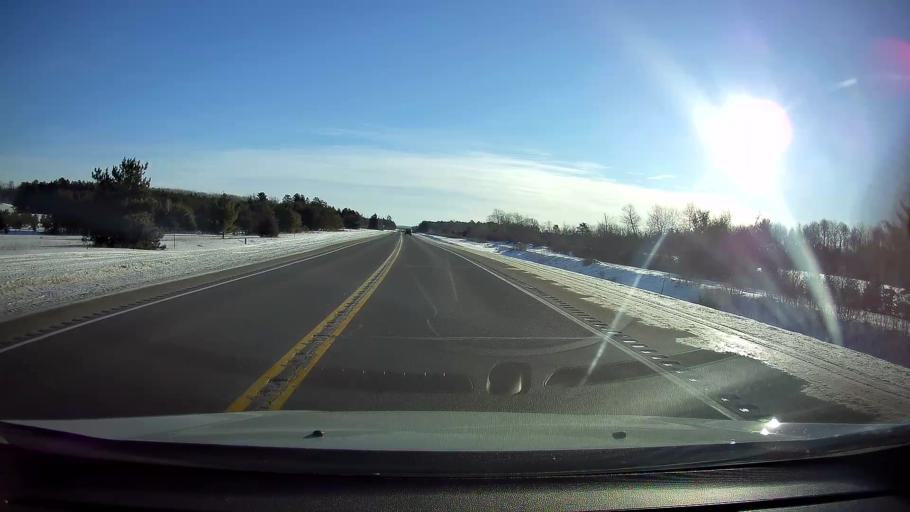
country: US
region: Wisconsin
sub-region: Sawyer County
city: Hayward
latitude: 45.9860
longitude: -91.5865
